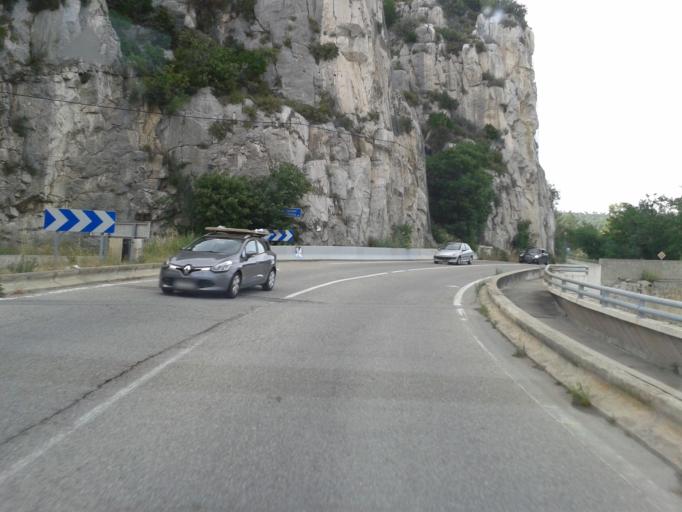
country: FR
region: Provence-Alpes-Cote d'Azur
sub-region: Departement du Vaucluse
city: Beaumont-de-Pertuis
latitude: 43.6907
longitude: 5.6674
